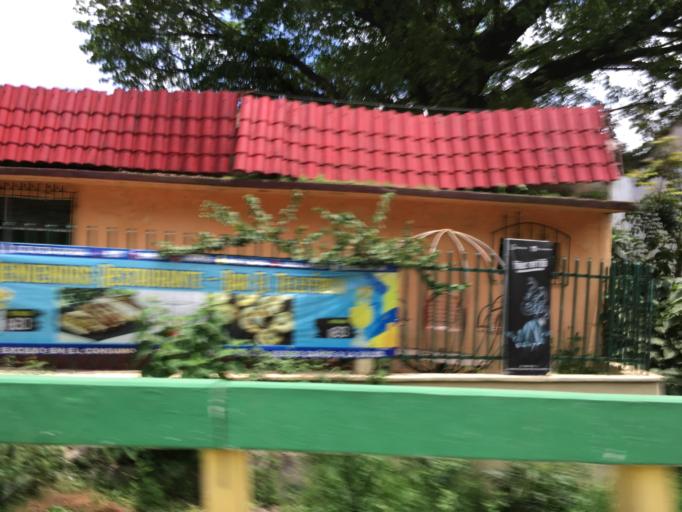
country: GT
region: Guatemala
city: Amatitlan
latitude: 14.4890
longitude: -90.6169
